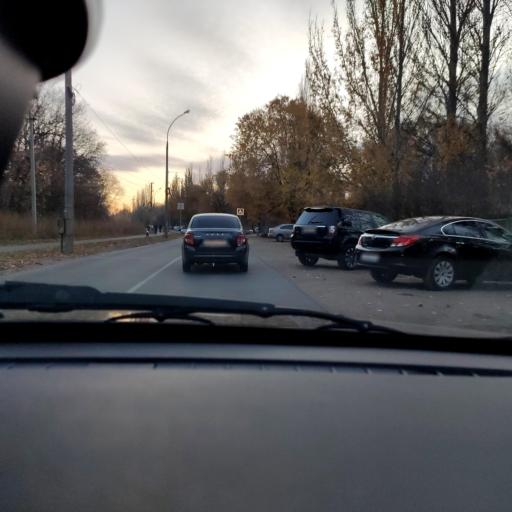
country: RU
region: Samara
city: Tol'yatti
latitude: 53.5141
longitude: 49.3110
